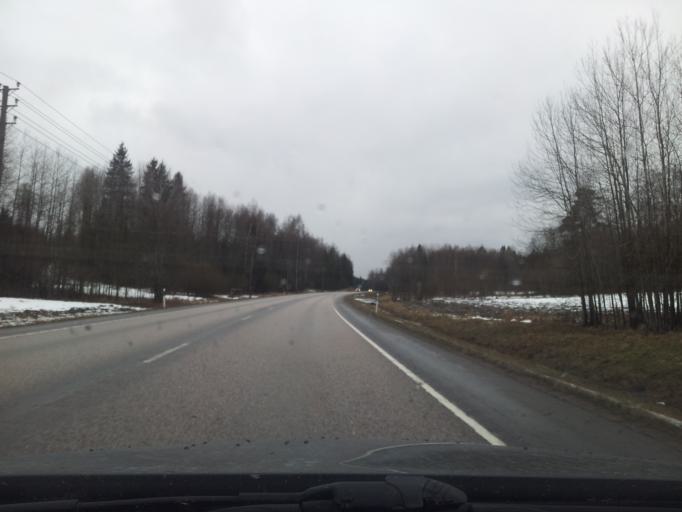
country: FI
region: Uusimaa
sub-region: Helsinki
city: Kirkkonummi
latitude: 60.1479
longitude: 24.5413
